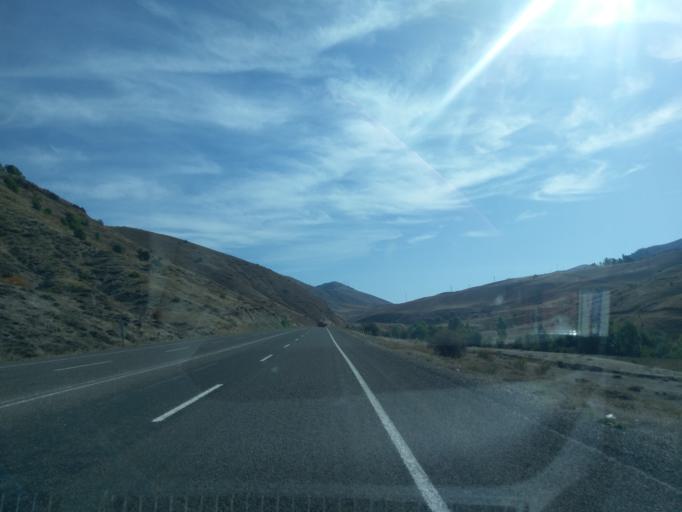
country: TR
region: Sivas
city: Akincilar
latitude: 39.8623
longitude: 38.3357
